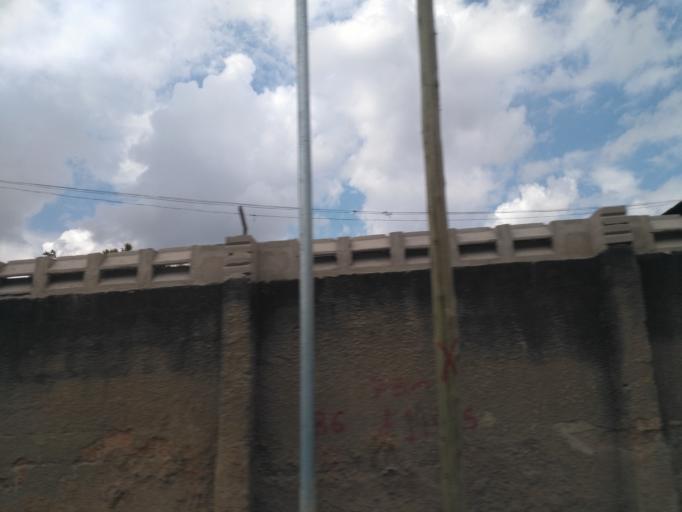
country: TZ
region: Dar es Salaam
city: Magomeni
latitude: -6.7626
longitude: 39.2426
